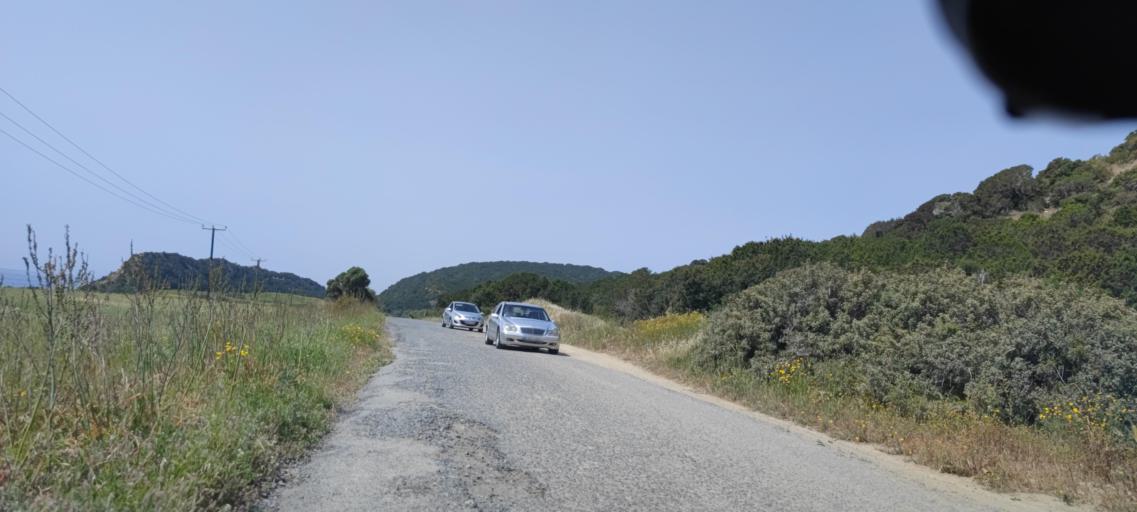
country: CY
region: Ammochostos
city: Rizokarpaso
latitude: 35.6238
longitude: 34.4776
